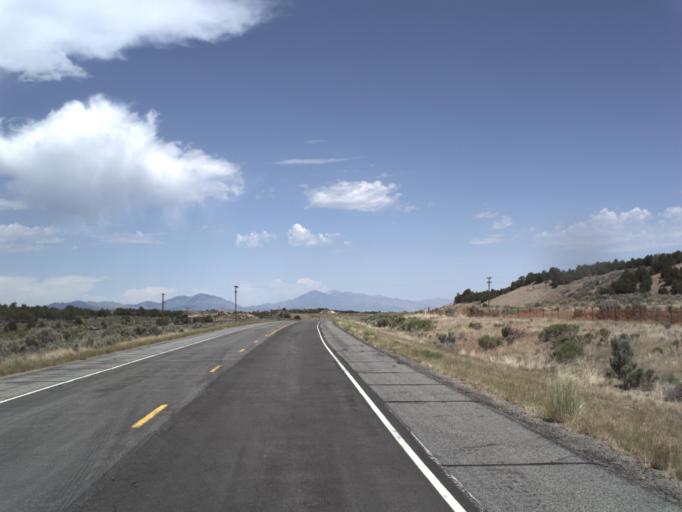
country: US
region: Utah
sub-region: Utah County
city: Genola
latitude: 39.9668
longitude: -112.2531
